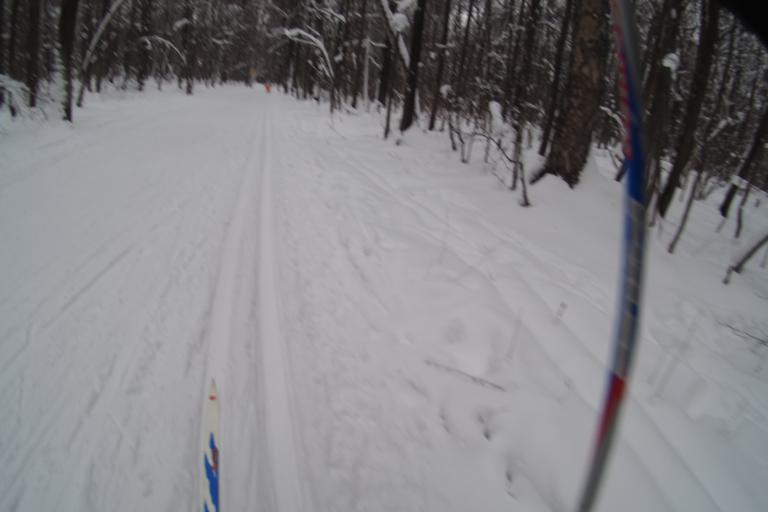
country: RU
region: Moscow
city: Ryazanskiy
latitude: 55.7676
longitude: 37.7714
